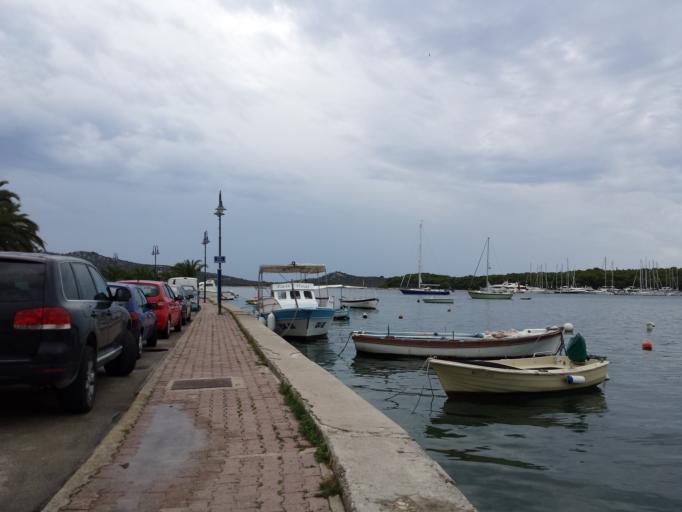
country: HR
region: Sibensko-Kniniska
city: Rogoznica
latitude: 43.5294
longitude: 15.9680
